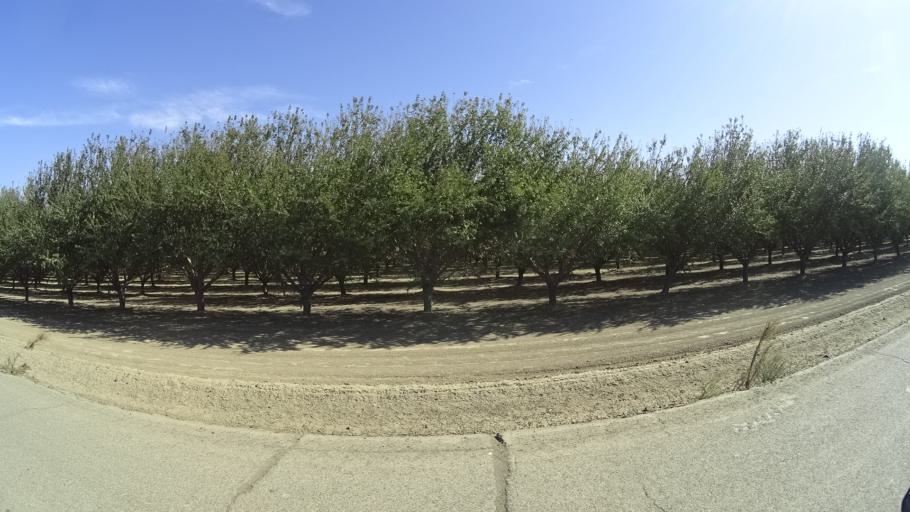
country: US
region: California
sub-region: Yolo County
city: Woodland
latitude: 38.6394
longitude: -121.7570
